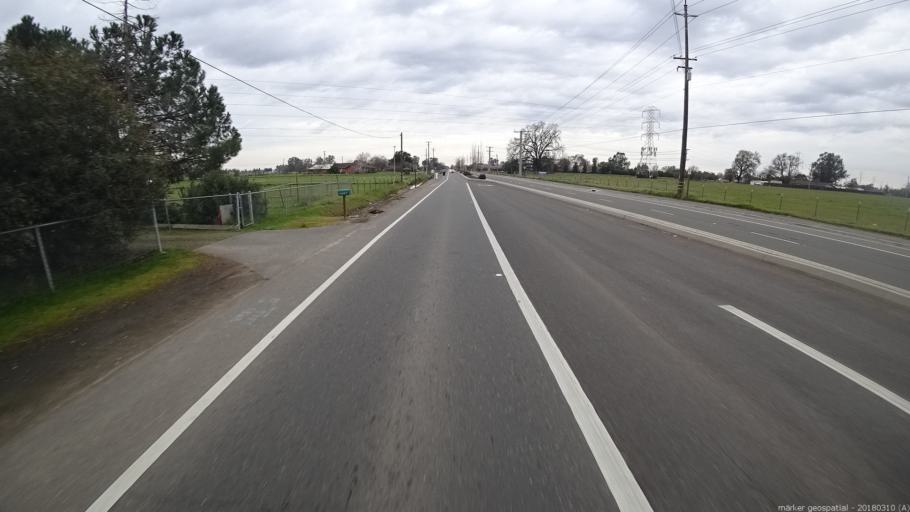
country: US
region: California
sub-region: Sacramento County
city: Vineyard
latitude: 38.4816
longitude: -121.3566
